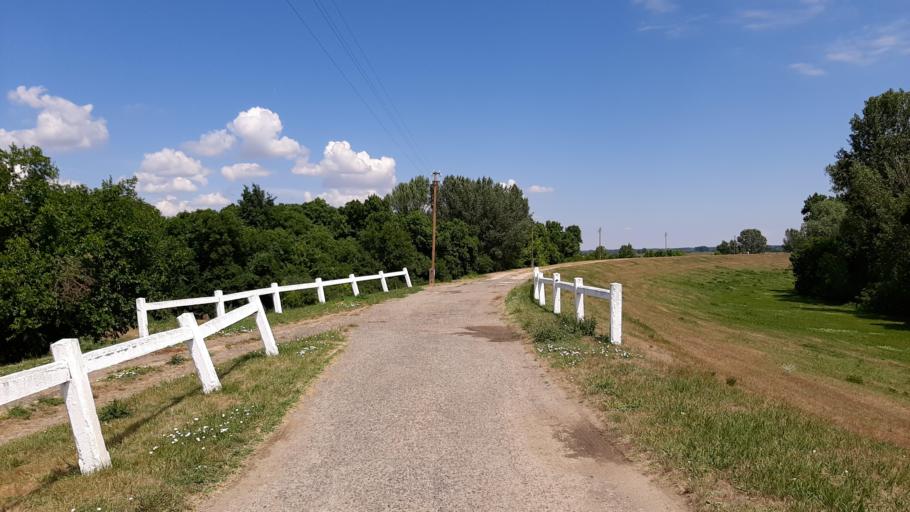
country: HU
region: Csongrad
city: Csanytelek
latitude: 46.6234
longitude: 20.1558
